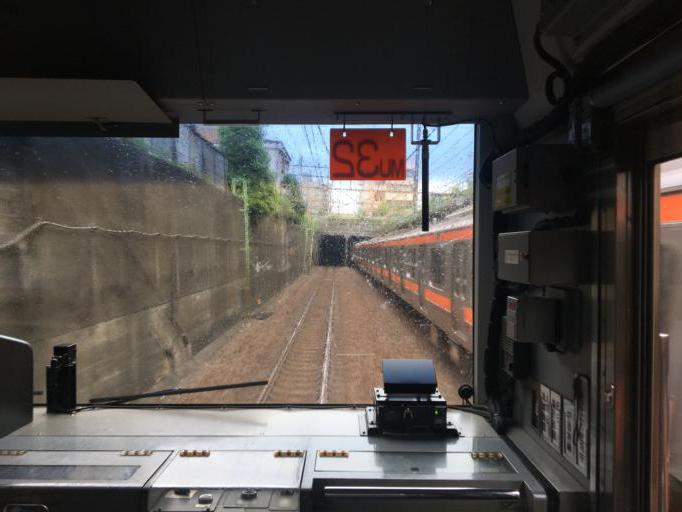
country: JP
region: Tokyo
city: Kokubunji
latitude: 35.6760
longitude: 139.4732
